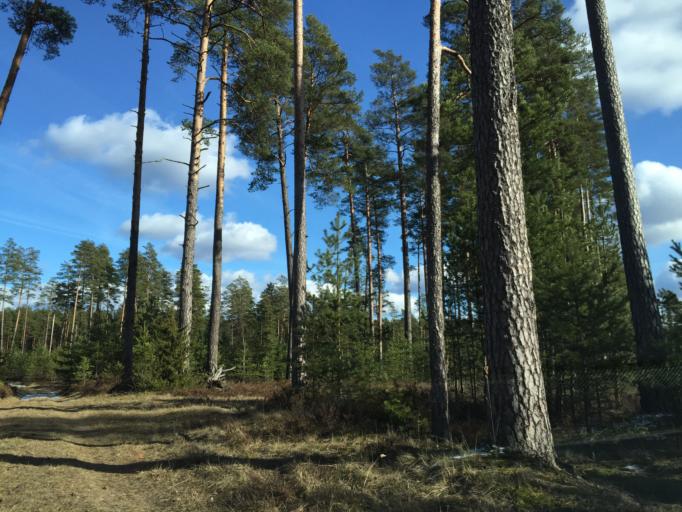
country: LV
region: Garkalne
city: Garkalne
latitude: 56.9646
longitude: 24.4449
